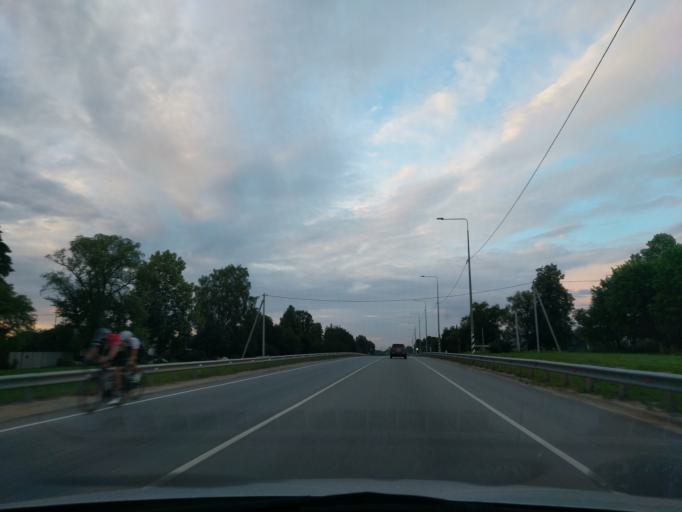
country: RU
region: Kaluga
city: Maloyaroslavets
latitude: 55.0301
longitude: 36.5233
